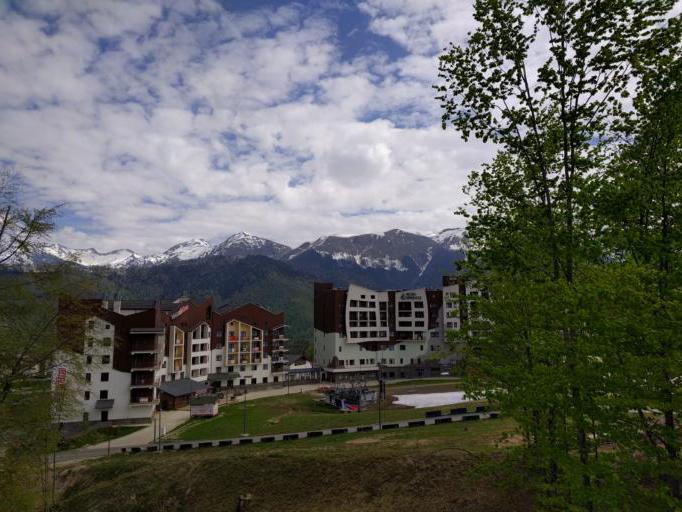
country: RU
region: Krasnodarskiy
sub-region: Sochi City
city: Krasnaya Polyana
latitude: 43.6598
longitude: 40.3170
